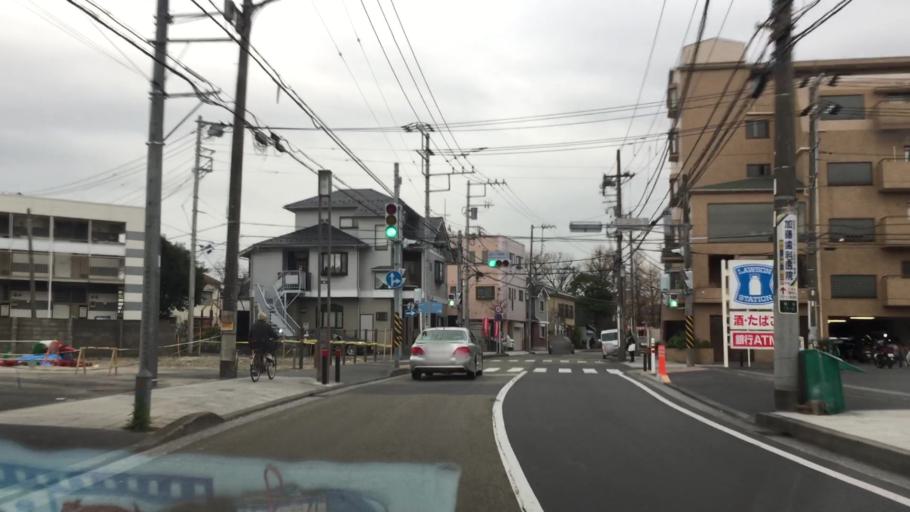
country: JP
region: Kanagawa
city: Zushi
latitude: 35.3394
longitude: 139.6269
